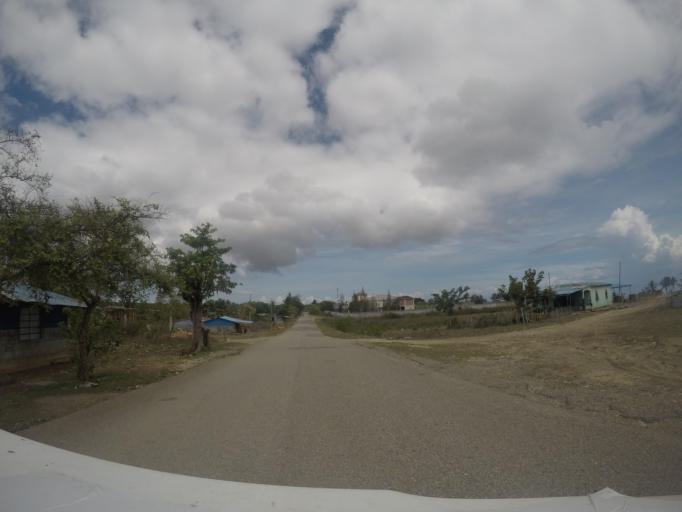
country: TL
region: Baucau
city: Baucau
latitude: -8.4653
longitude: 126.4312
